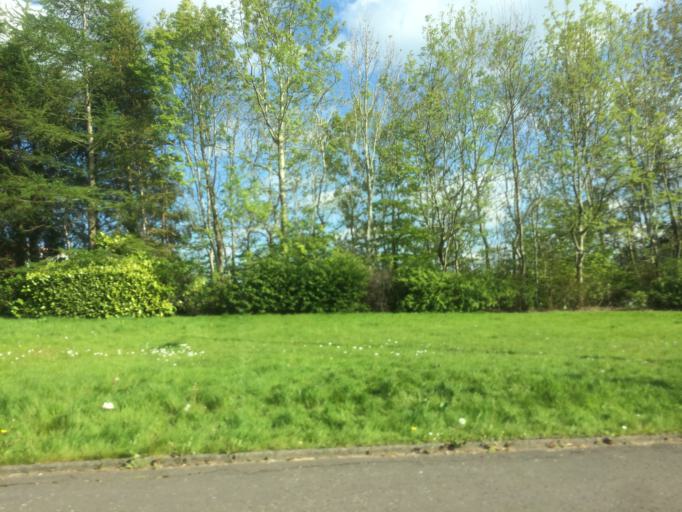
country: GB
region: Scotland
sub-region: East Renfrewshire
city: Newton Mearns
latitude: 55.8031
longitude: -4.3414
